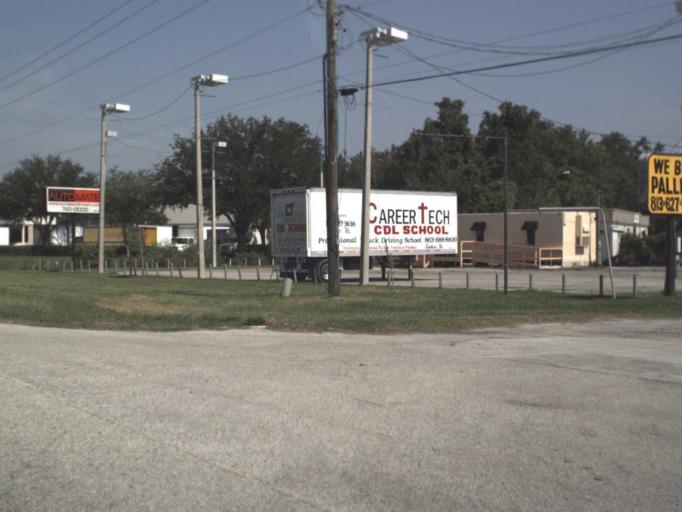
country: US
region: Florida
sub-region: Hillsborough County
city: Palm River-Clair Mel
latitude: 27.9512
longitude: -82.3626
